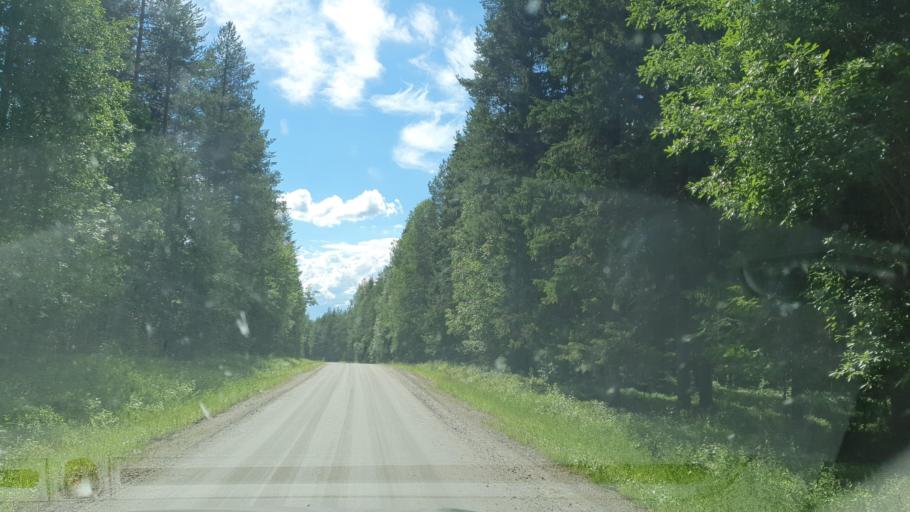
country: FI
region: Kainuu
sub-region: Kehys-Kainuu
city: Kuhmo
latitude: 64.1655
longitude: 29.8618
